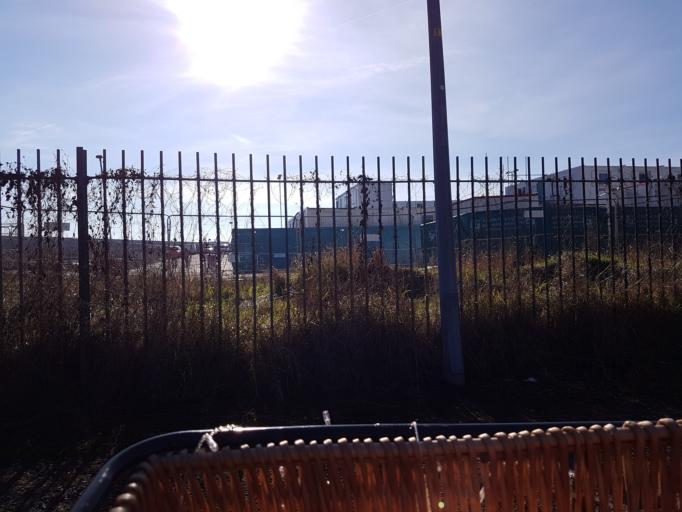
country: GB
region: England
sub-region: Cambridgeshire
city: Fulbourn
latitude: 52.1827
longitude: 0.1751
